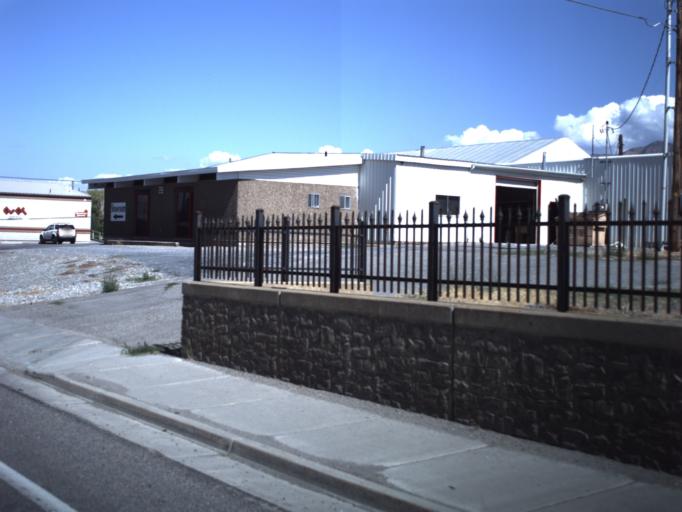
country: US
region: Utah
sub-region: Cache County
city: Richmond
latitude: 41.9230
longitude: -111.8143
